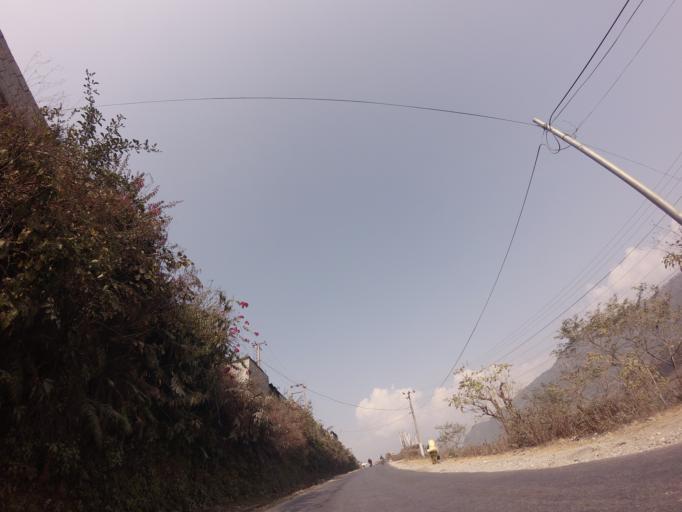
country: NP
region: Western Region
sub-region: Gandaki Zone
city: Pokhara
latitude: 28.2622
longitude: 83.9578
